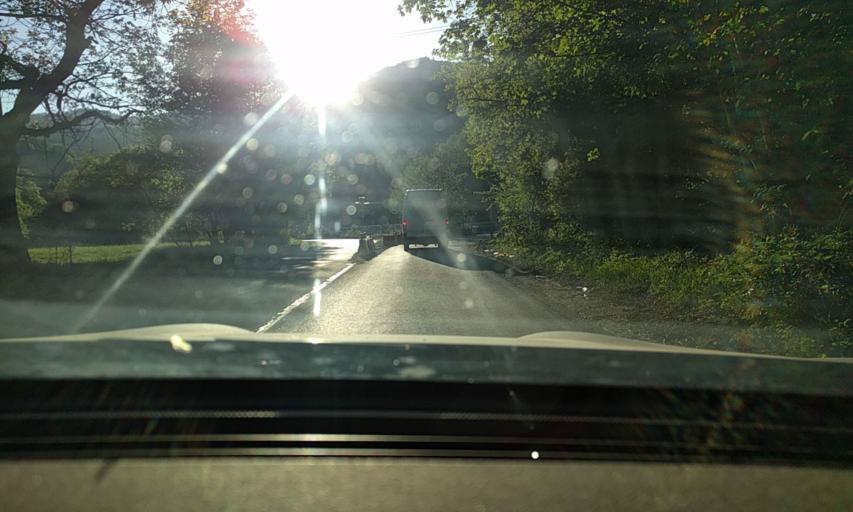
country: RO
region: Bacau
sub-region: Oras Slanic-Moldova
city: Slanic-Moldova
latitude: 46.1204
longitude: 26.4347
